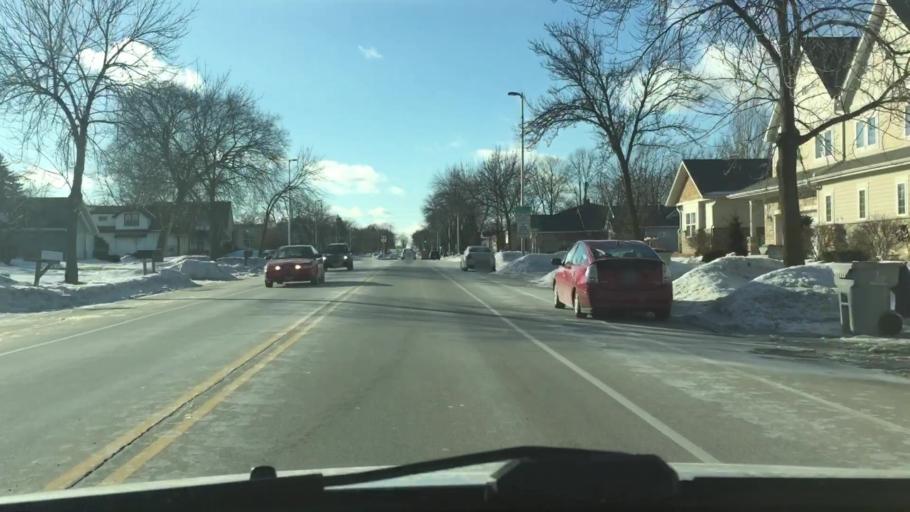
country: US
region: Wisconsin
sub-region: Milwaukee County
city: West Milwaukee
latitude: 42.9740
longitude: -87.9652
